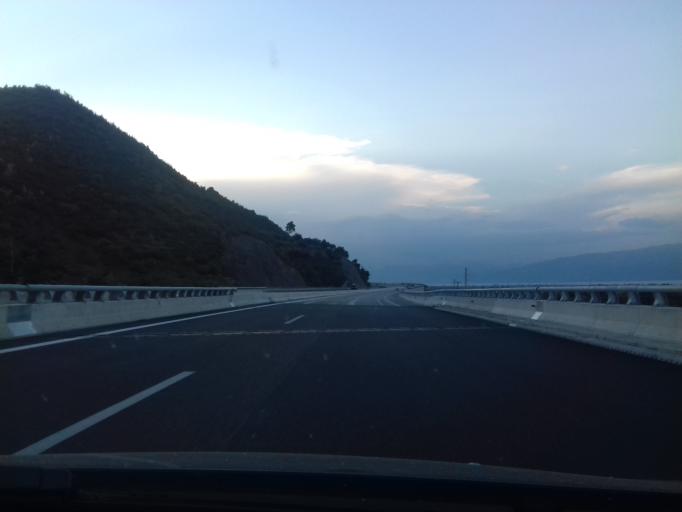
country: GR
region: West Greece
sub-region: Nomos Achaias
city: Temeni
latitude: 38.1961
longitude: 22.1527
